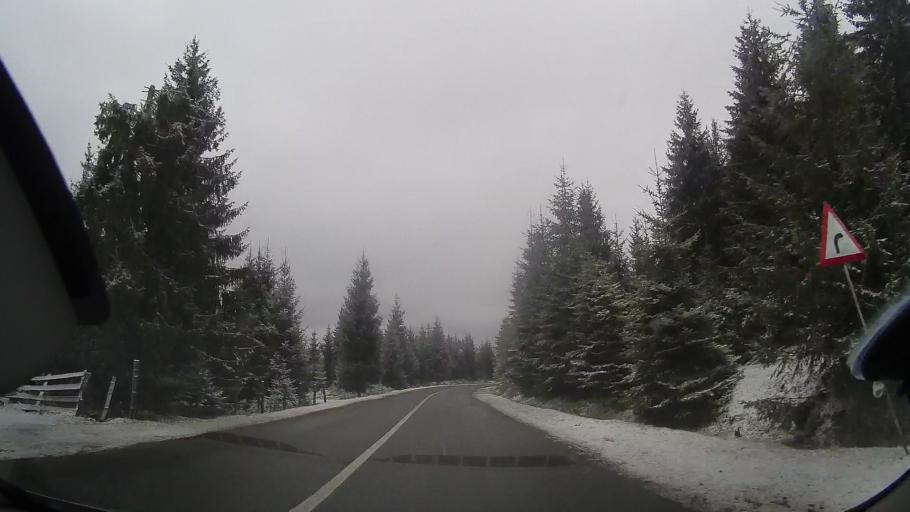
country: RO
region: Cluj
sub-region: Comuna Belis
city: Belis
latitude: 46.6884
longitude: 23.0354
